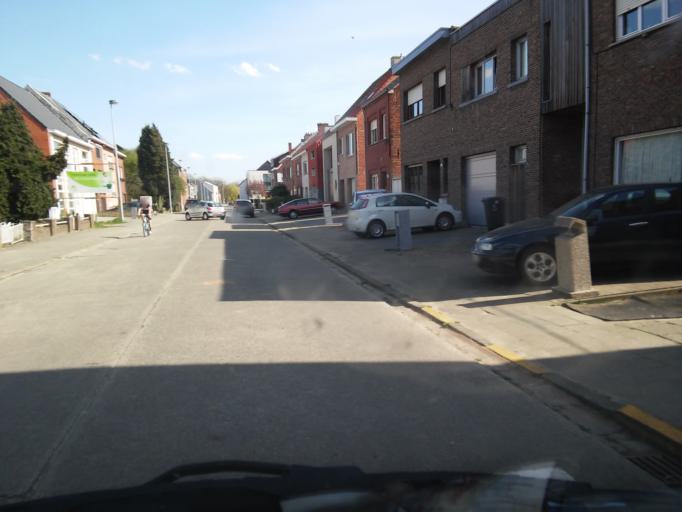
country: BE
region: Flanders
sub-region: Provincie Antwerpen
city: Willebroek
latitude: 51.0558
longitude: 4.3774
